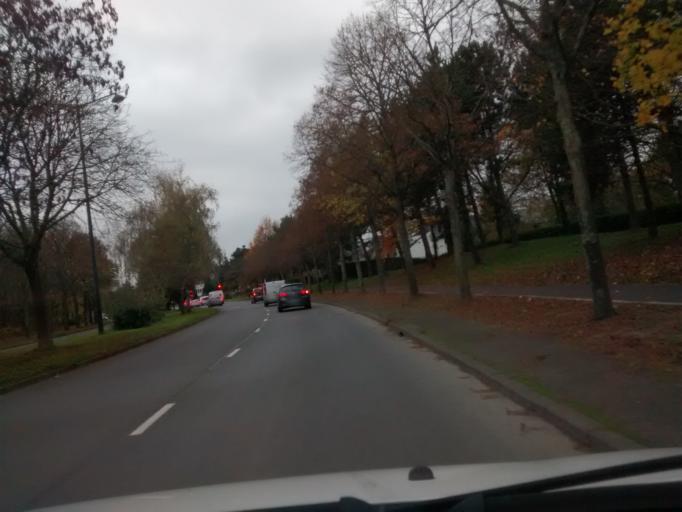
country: FR
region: Brittany
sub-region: Departement d'Ille-et-Vilaine
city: Rennes
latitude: 48.1311
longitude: -1.6702
